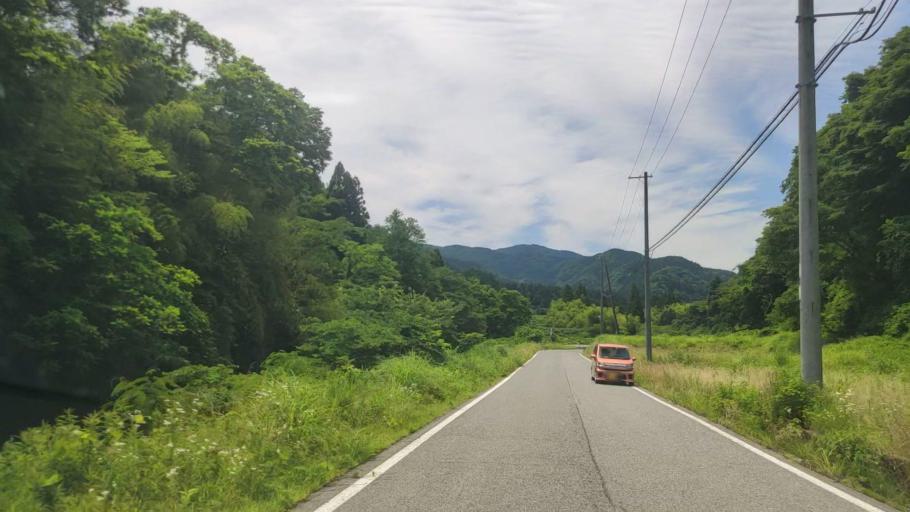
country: JP
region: Tottori
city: Tottori
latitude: 35.4305
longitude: 134.5304
